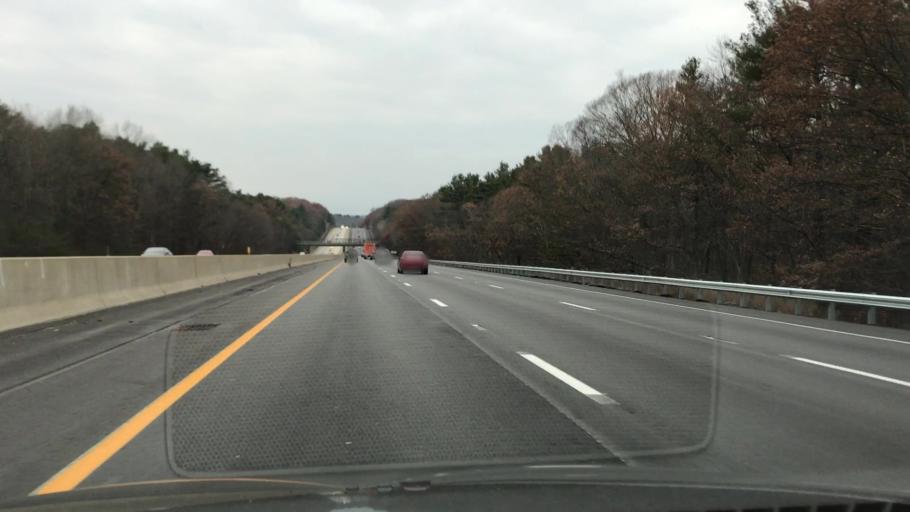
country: US
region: Massachusetts
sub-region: Worcester County
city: Grafton
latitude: 42.2272
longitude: -71.6765
